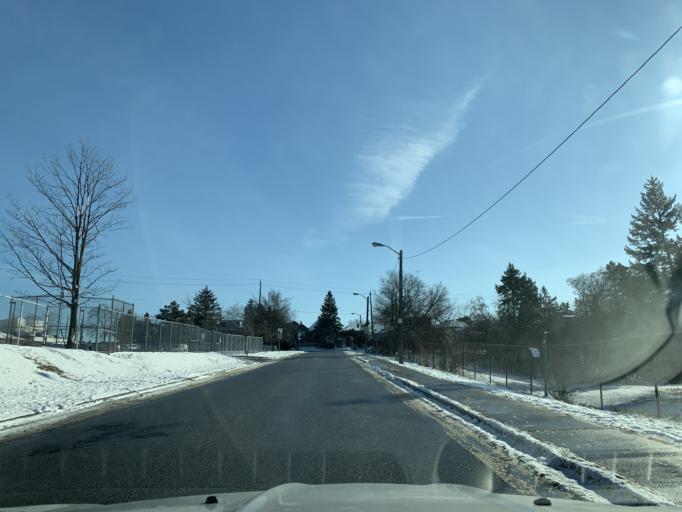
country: CA
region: Ontario
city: Toronto
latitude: 43.6814
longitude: -79.4785
